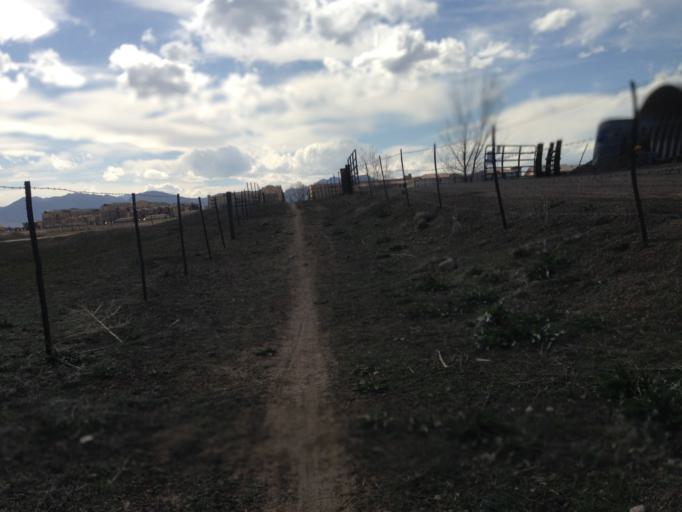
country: US
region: Colorado
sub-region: Broomfield County
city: Broomfield
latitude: 39.9433
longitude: -105.1136
